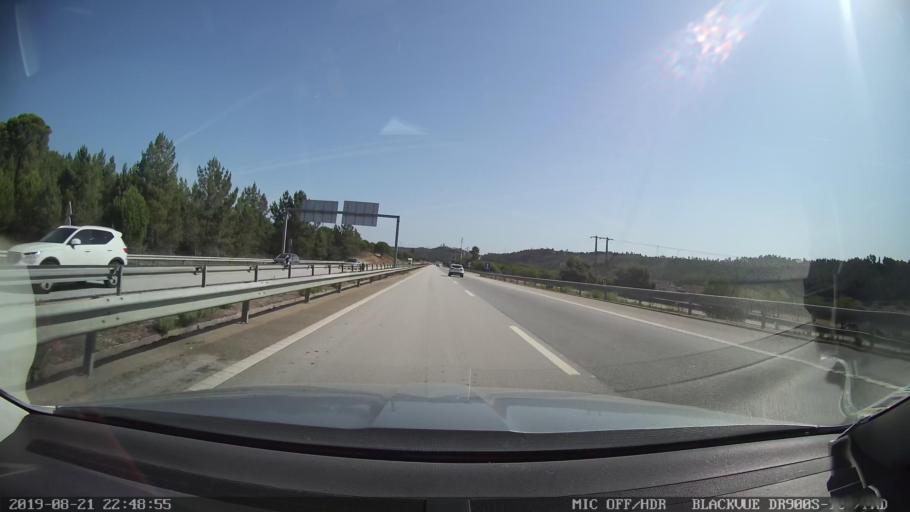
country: PT
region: Santarem
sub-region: Abrantes
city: Abrantes
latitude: 39.4811
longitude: -8.2253
